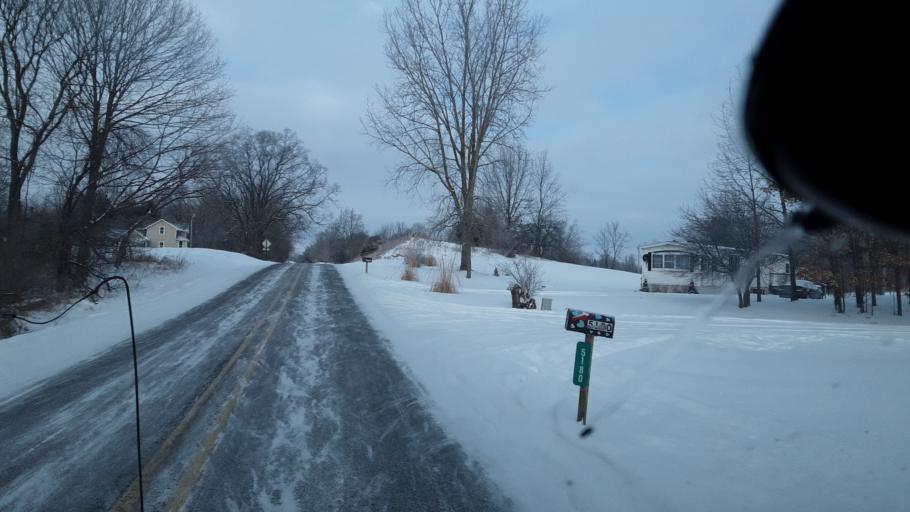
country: US
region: Michigan
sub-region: Ingham County
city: Leslie
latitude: 42.3685
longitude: -84.4835
